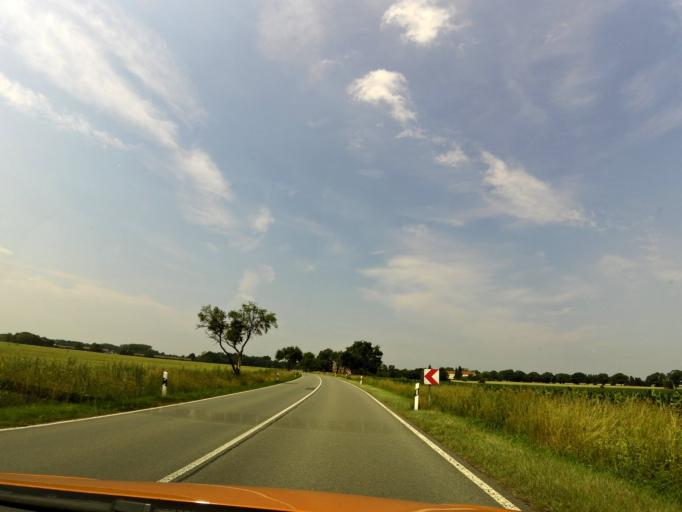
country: DE
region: Brandenburg
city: Gumtow
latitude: 53.0049
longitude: 12.3331
